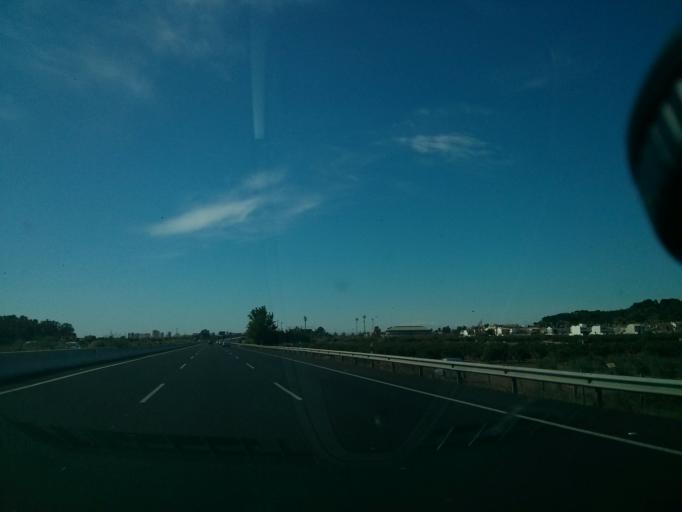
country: ES
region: Valencia
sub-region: Provincia de Valencia
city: Puig
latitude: 39.5987
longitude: -0.2933
